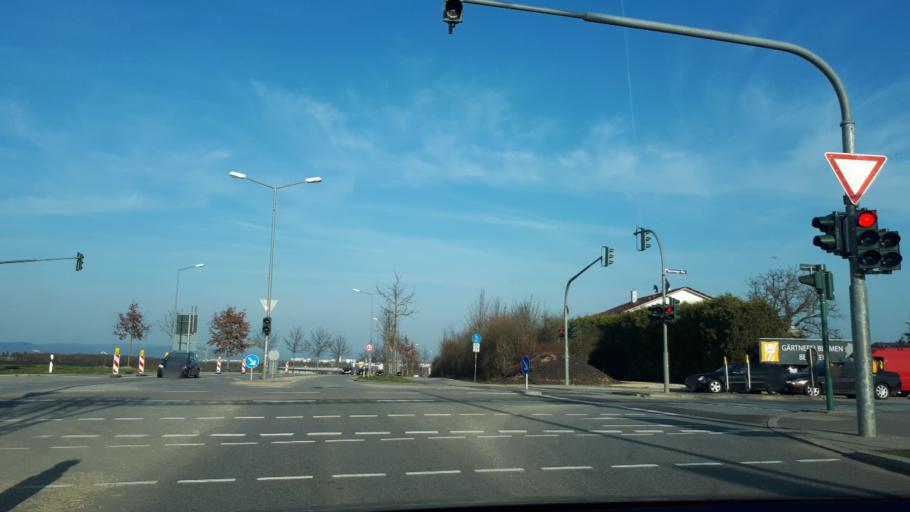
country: DE
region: Bavaria
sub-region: Upper Palatinate
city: Regensburg
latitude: 48.9909
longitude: 12.1125
